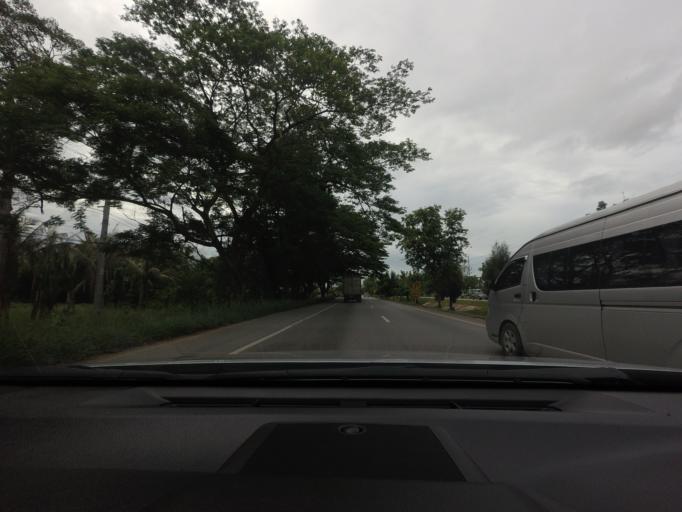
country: TH
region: Prachuap Khiri Khan
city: Hua Hin
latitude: 12.6199
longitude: 99.8590
